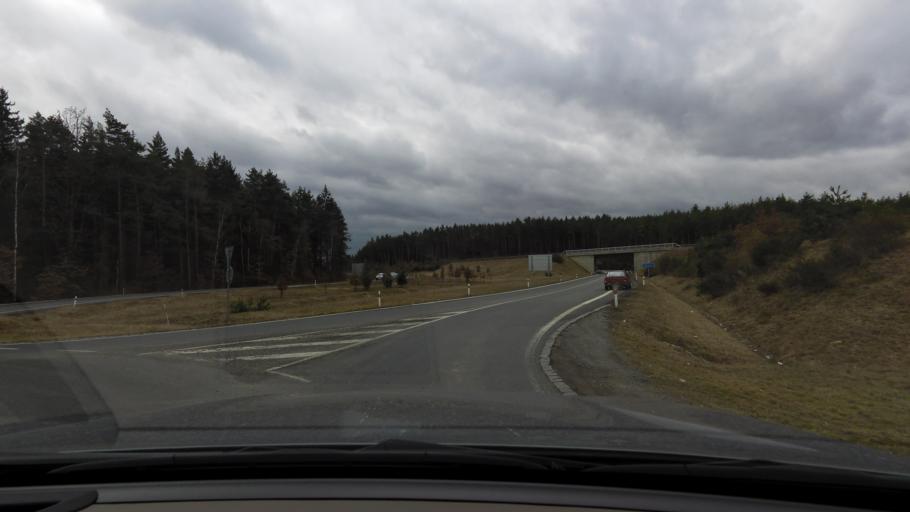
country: CZ
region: Plzensky
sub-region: Okres Plzen-Sever
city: Tremosna
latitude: 49.8051
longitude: 13.3896
